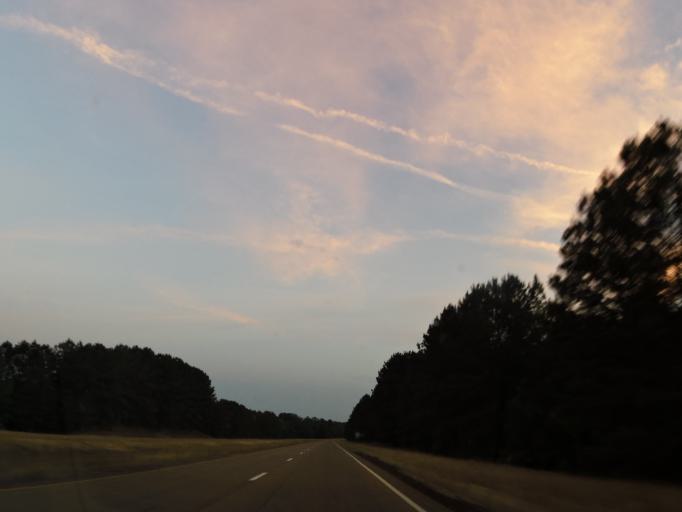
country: US
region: Mississippi
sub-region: Lauderdale County
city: Meridian Station
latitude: 32.6089
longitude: -88.4990
